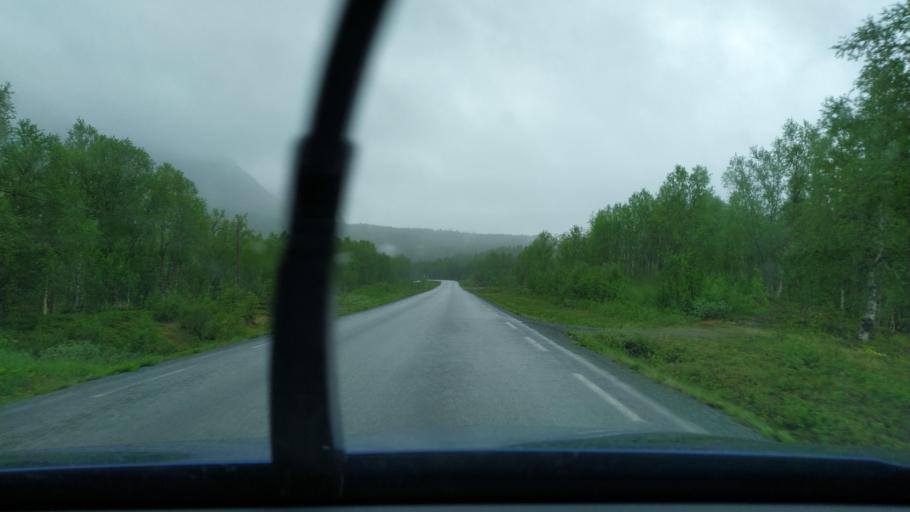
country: NO
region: Troms
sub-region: Dyroy
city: Brostadbotn
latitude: 69.0251
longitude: 17.7383
